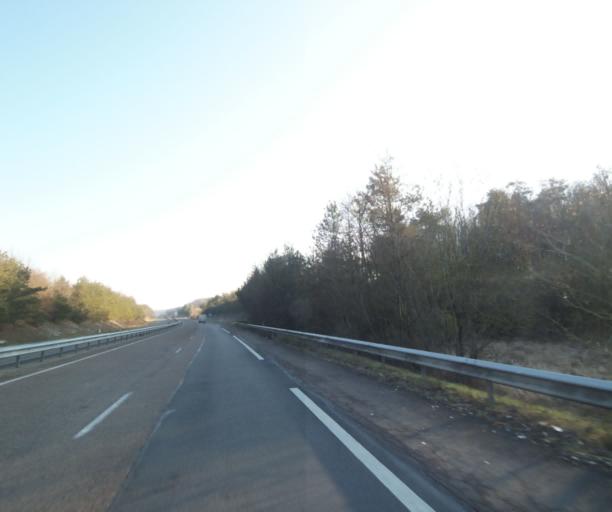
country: FR
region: Champagne-Ardenne
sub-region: Departement de la Haute-Marne
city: Chevillon
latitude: 48.5099
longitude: 5.0954
